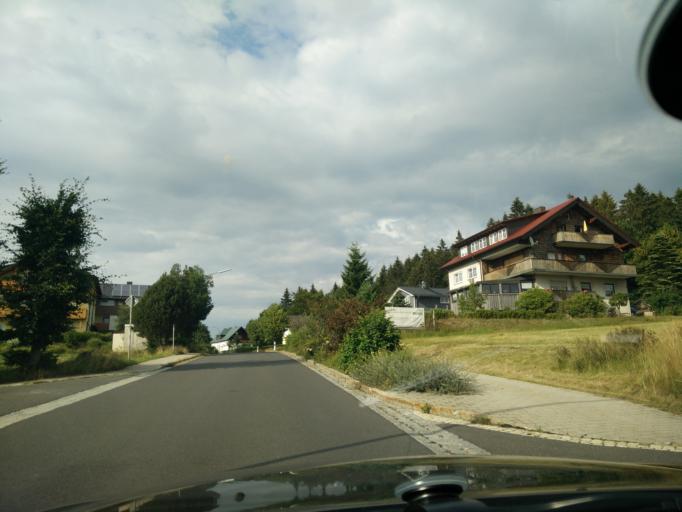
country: DE
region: Bavaria
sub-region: Upper Franconia
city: Fichtelberg
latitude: 50.0141
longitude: 11.8524
